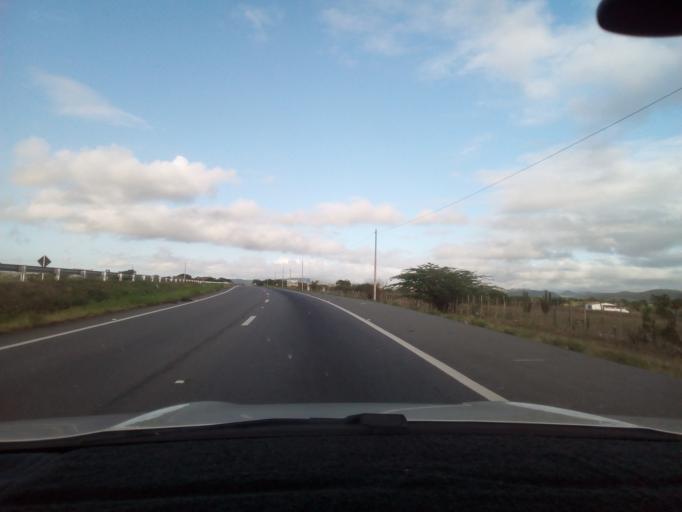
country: BR
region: Paraiba
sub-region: Serra Redonda
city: Alagoa Grande
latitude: -7.2022
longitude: -35.5561
